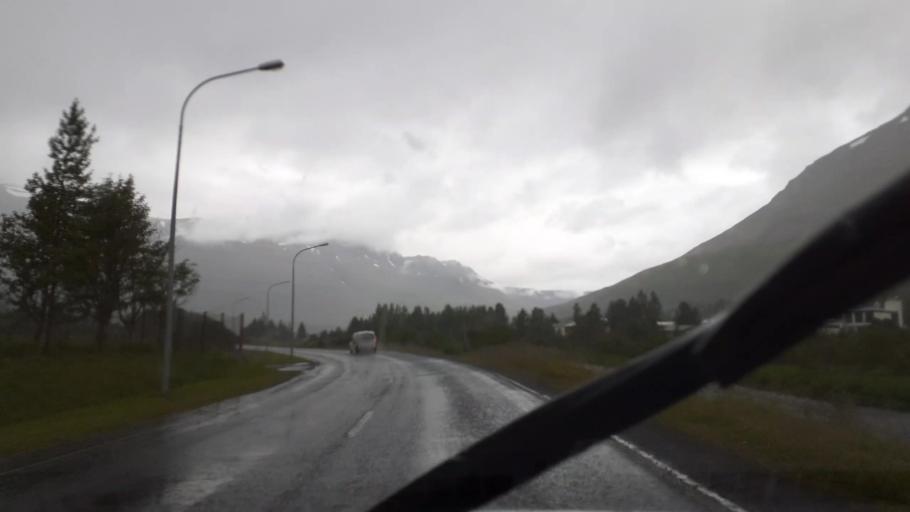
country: IS
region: East
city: Eskifjoerdur
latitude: 65.2548
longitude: -14.0142
